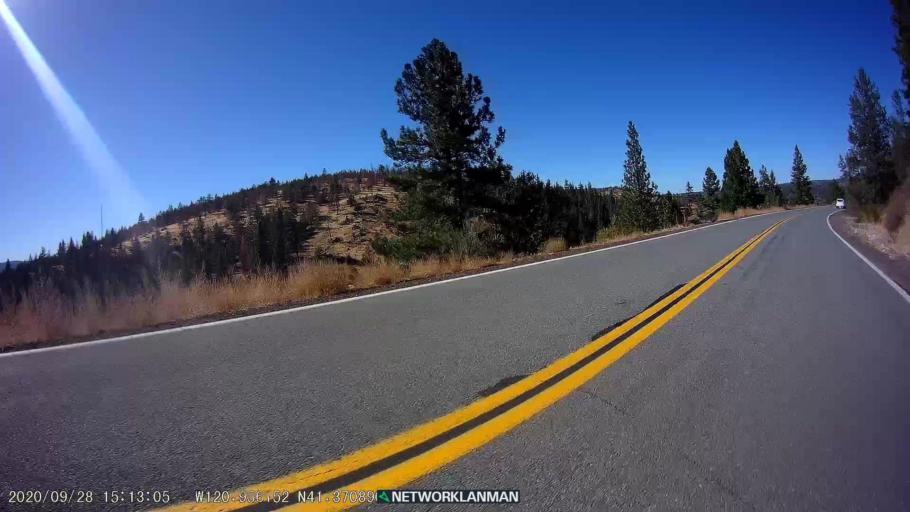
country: US
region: California
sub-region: Modoc County
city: Alturas
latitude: 41.3711
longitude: -120.9562
